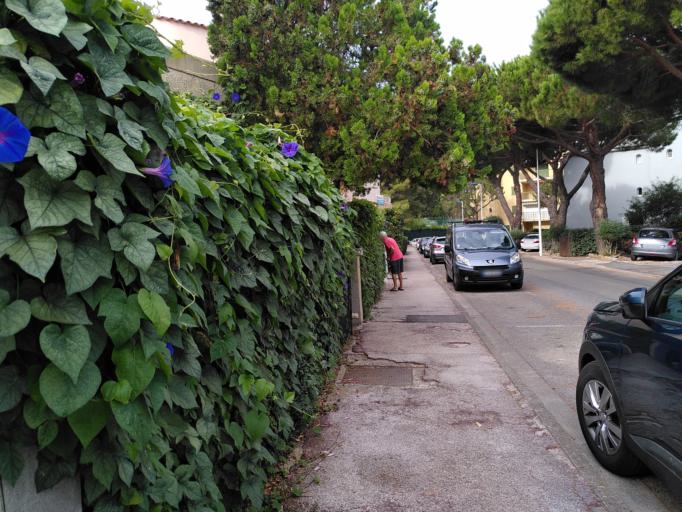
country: FR
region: Provence-Alpes-Cote d'Azur
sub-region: Departement du Var
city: Cavalaire-sur-Mer
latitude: 43.1696
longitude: 6.5329
